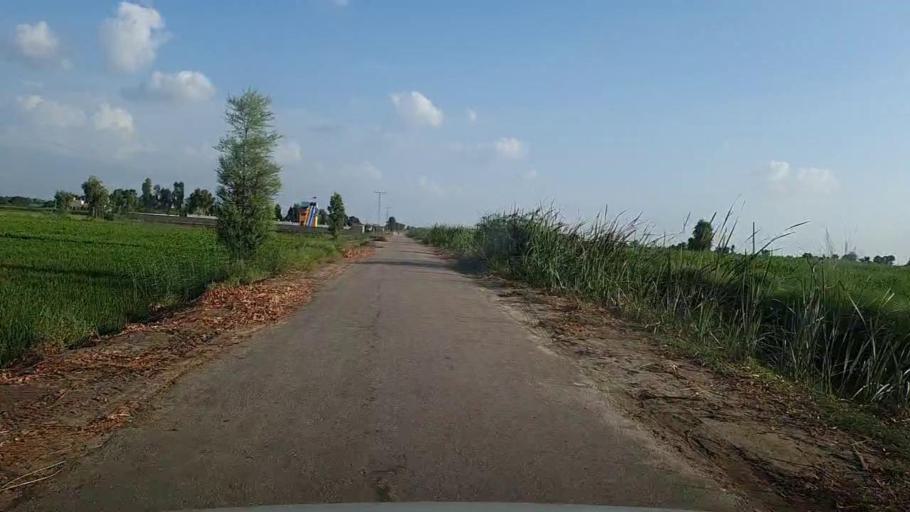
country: PK
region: Sindh
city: Hingorja
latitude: 27.0913
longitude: 68.4025
